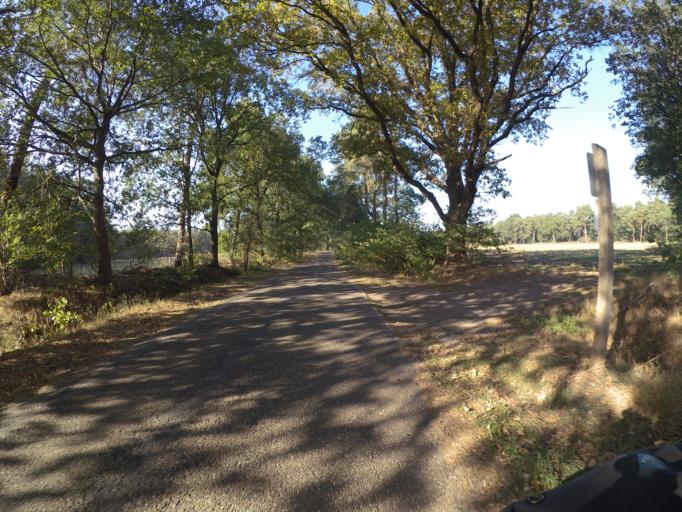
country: NL
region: North Brabant
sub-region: Gemeente Oirschot
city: Oirschot
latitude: 51.4838
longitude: 5.3241
